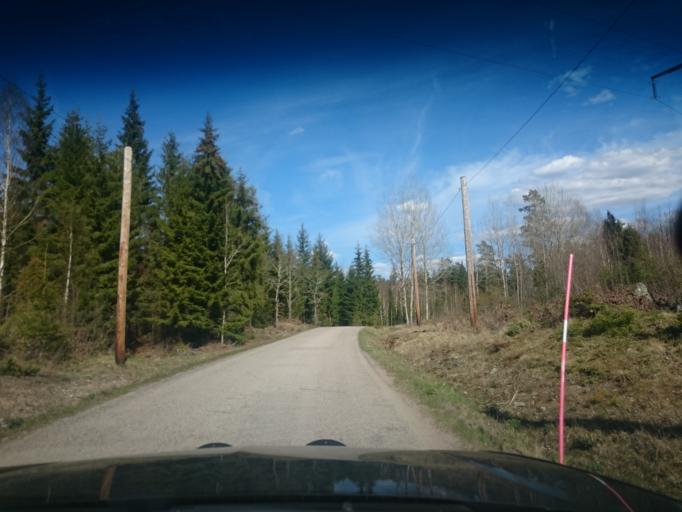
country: SE
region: Kalmar
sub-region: Hultsfreds Kommun
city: Virserum
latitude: 57.3579
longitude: 15.4991
